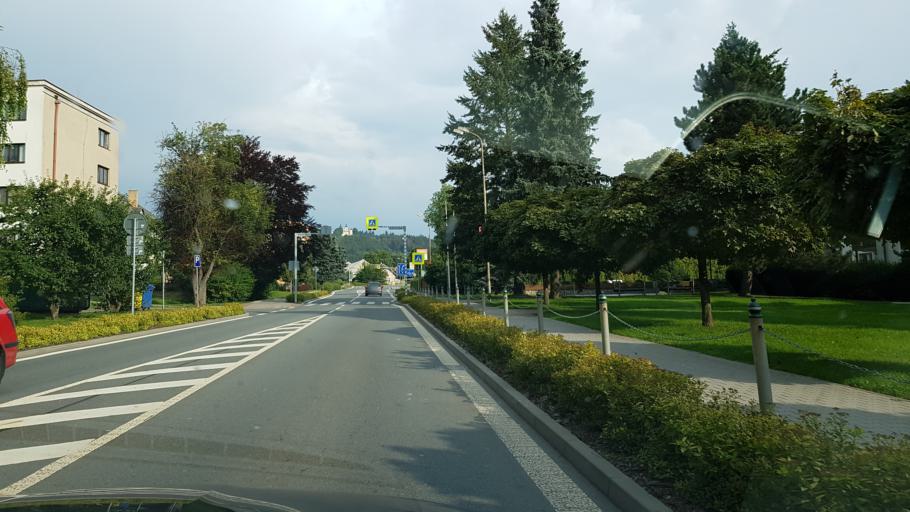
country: CZ
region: Pardubicky
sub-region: Okres Usti nad Orlici
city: Kraliky
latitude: 50.0831
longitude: 16.7588
